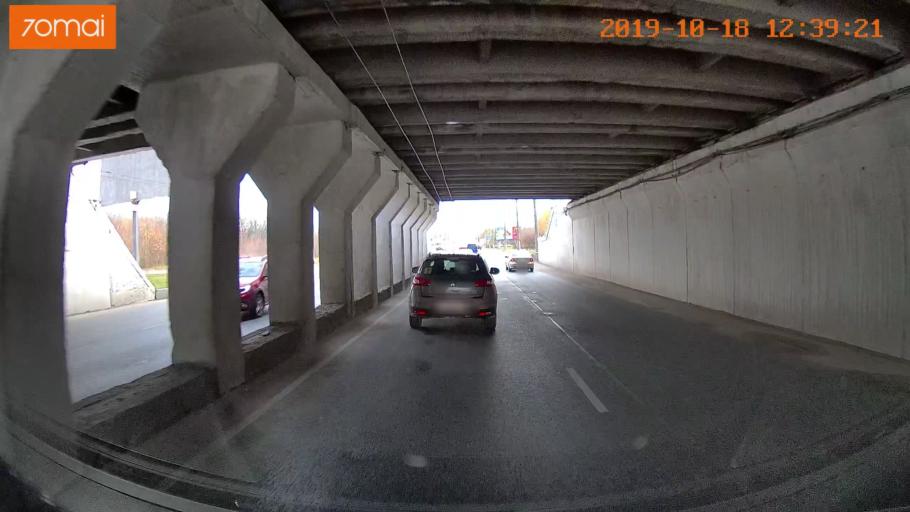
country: RU
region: Rjazan
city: Ryazan'
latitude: 54.6507
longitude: 39.6432
